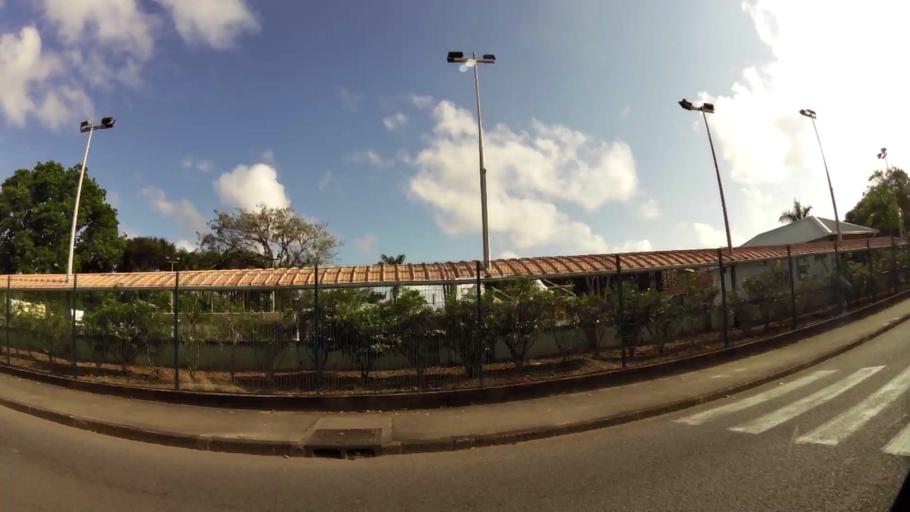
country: GF
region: Guyane
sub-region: Guyane
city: Cayenne
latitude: 4.9391
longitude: -52.3190
